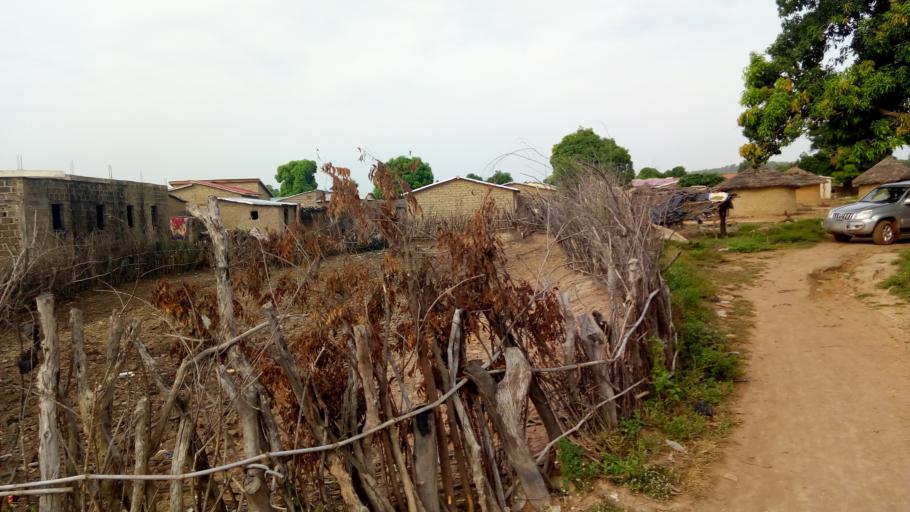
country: ML
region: Koulikoro
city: Kangaba
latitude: 11.6433
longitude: -8.7529
